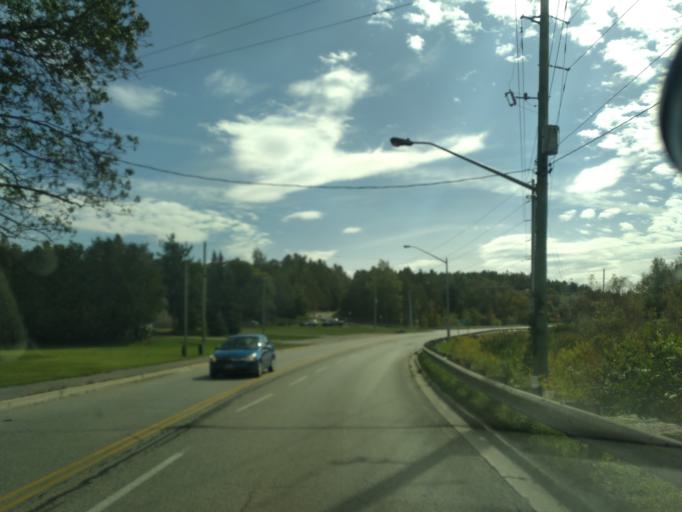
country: CA
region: Ontario
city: Newmarket
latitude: 44.0928
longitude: -79.4895
